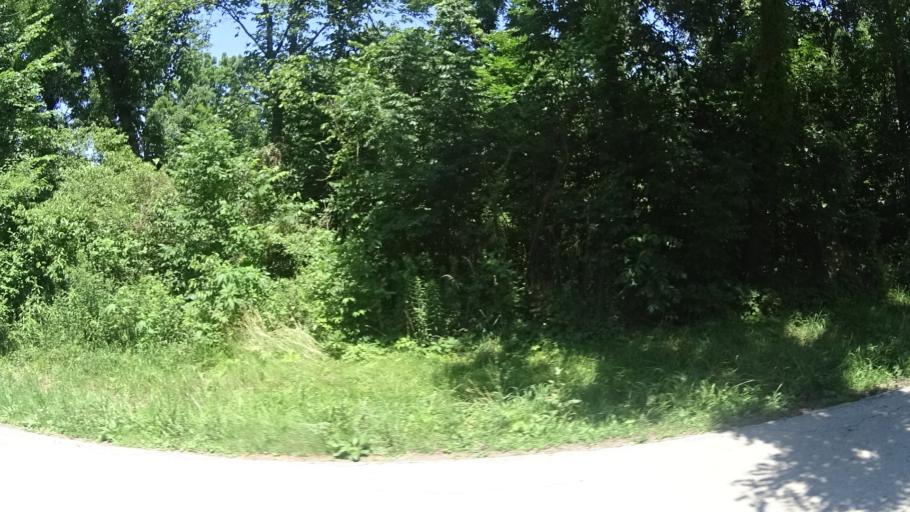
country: US
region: Ohio
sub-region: Lorain County
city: Vermilion
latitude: 41.3390
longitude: -82.3751
